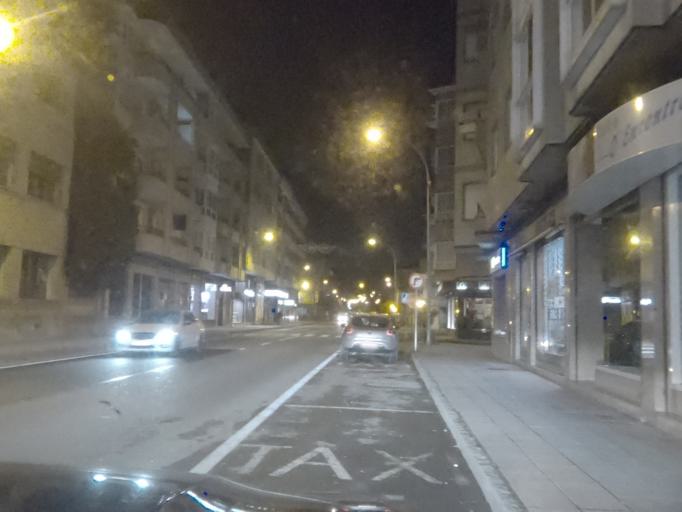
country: ES
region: Galicia
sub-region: Provincia de Ourense
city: Verin
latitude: 41.9398
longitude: -7.4357
